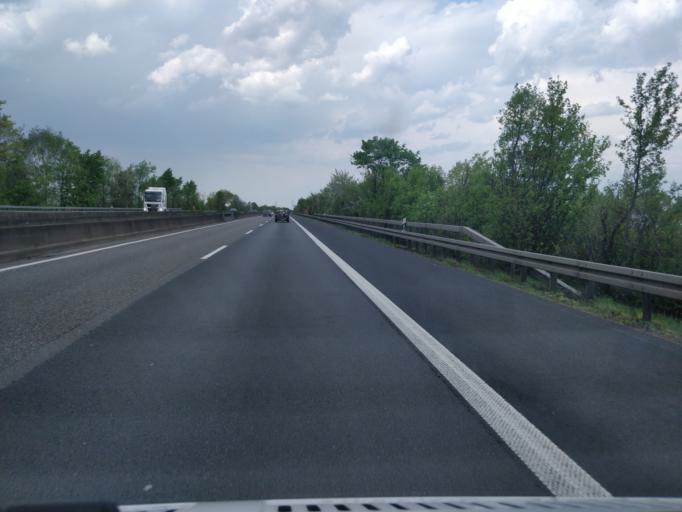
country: DE
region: North Rhine-Westphalia
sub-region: Regierungsbezirk Koln
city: Euskirchen
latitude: 50.7079
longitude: 6.7741
